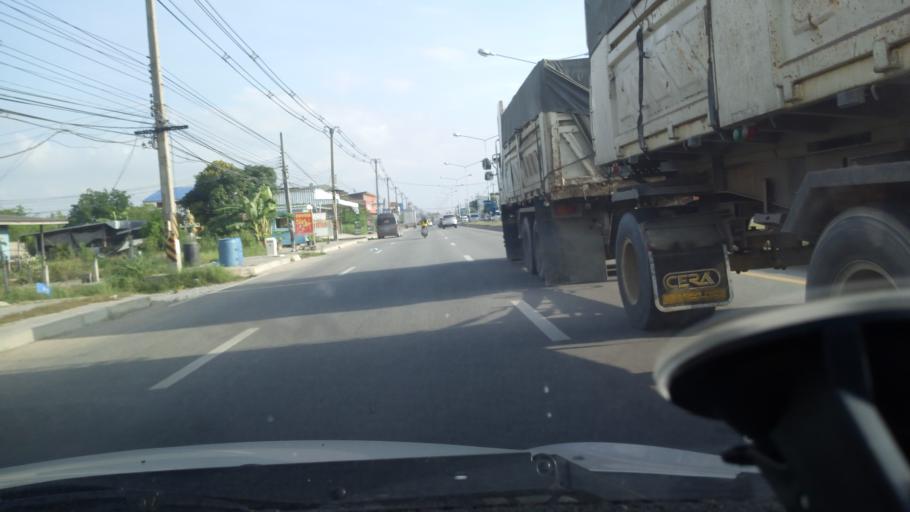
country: TH
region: Chon Buri
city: Phan Thong
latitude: 13.4334
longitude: 101.1078
